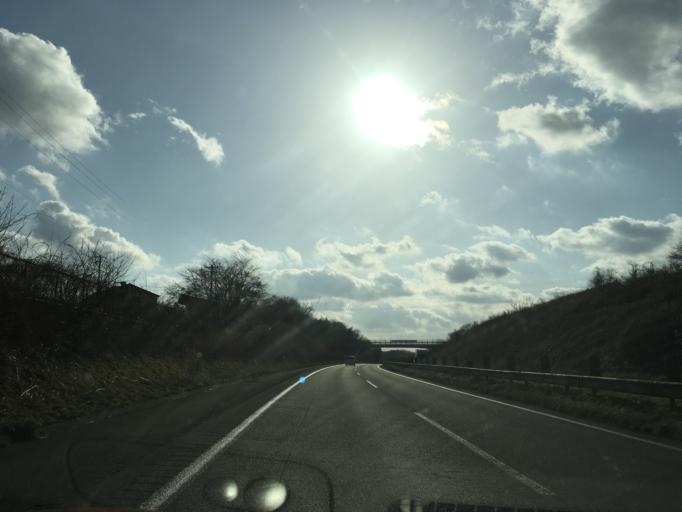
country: JP
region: Miyagi
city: Furukawa
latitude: 38.7054
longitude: 140.9962
